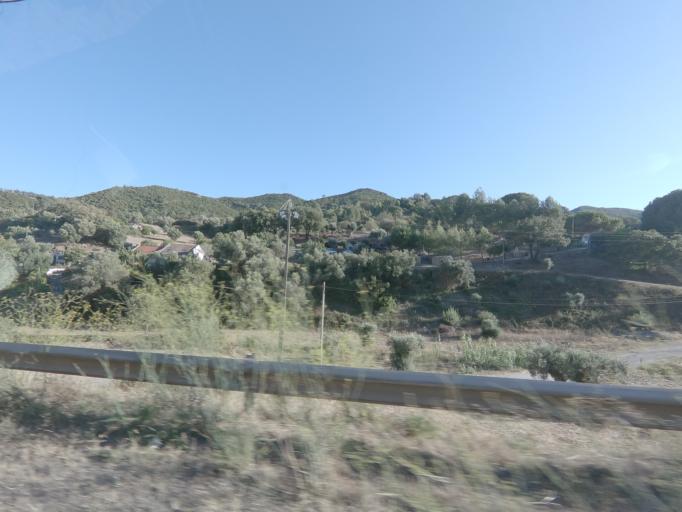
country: PT
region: Setubal
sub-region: Palmela
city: Quinta do Anjo
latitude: 38.5051
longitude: -8.9546
